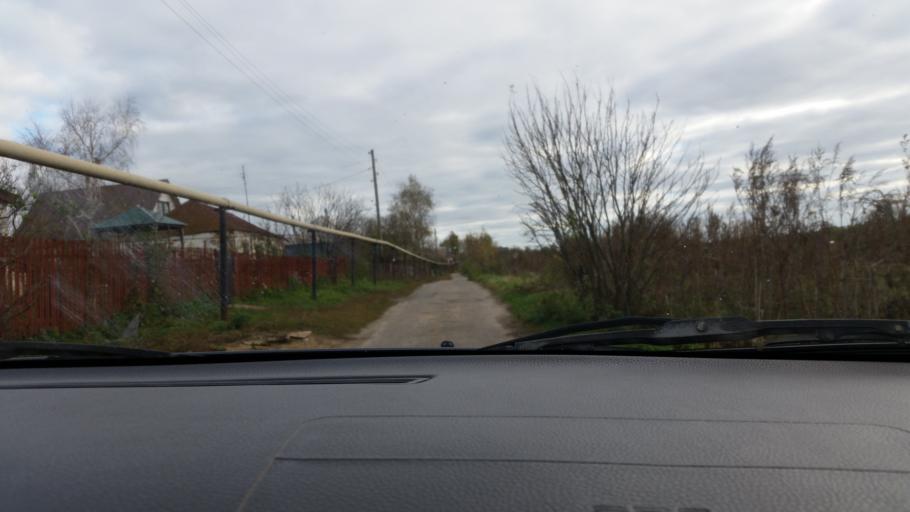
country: RU
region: Lipetsk
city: Gryazi
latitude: 52.4533
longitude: 39.9816
